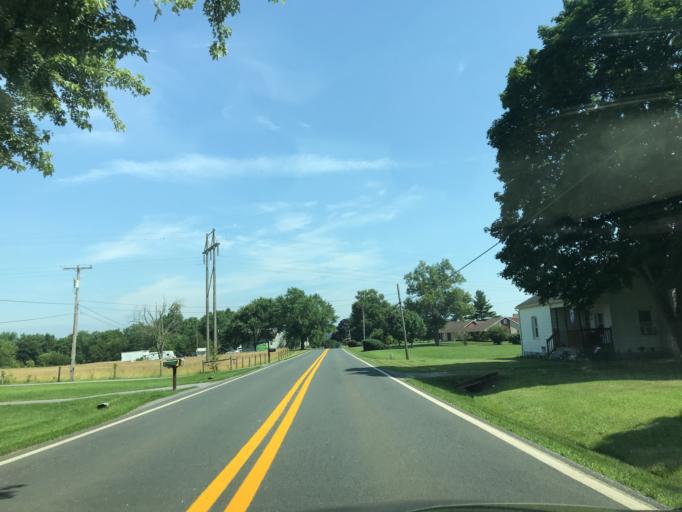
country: US
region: Maryland
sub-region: Carroll County
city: Taneytown
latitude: 39.6367
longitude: -77.1564
